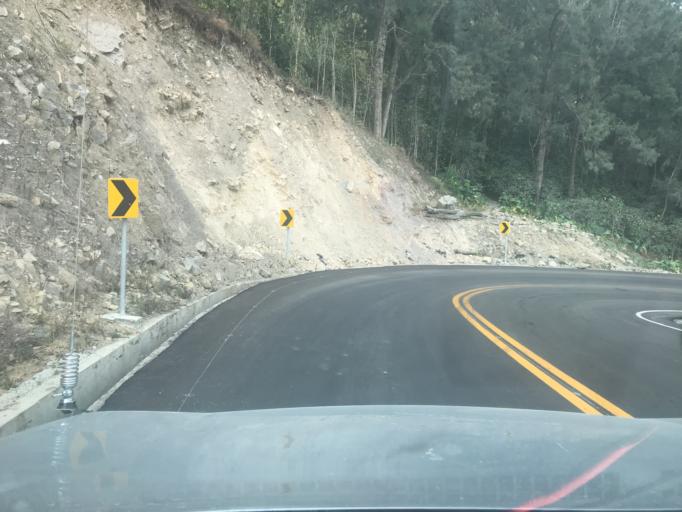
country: TL
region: Manufahi
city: Same
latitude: -8.8925
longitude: 125.5944
